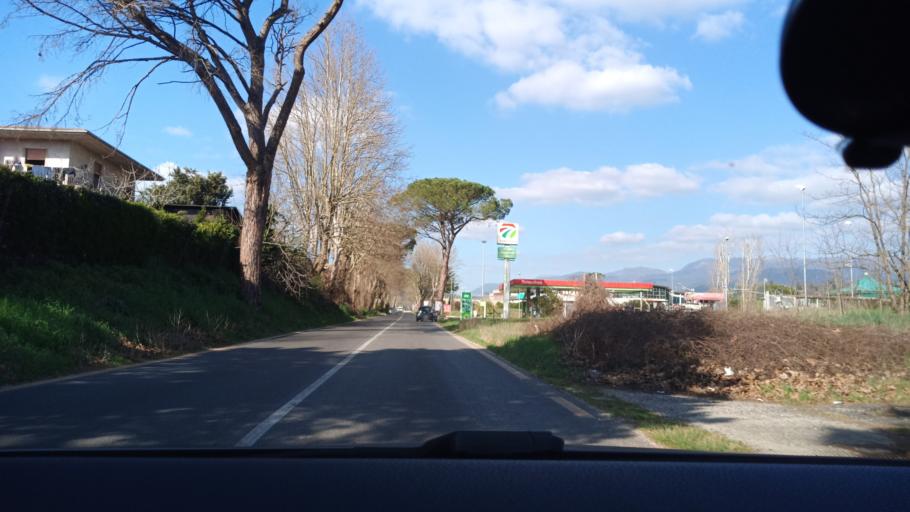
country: IT
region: Latium
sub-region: Citta metropolitana di Roma Capitale
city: Torrita Tiberina
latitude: 42.2513
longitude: 12.6369
